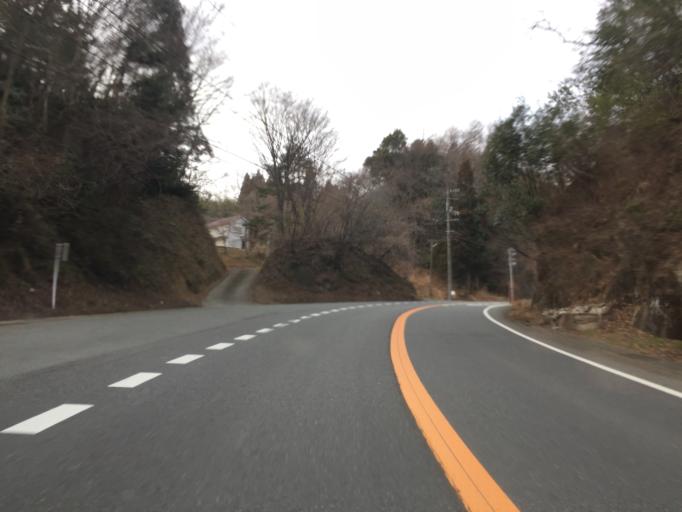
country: JP
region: Fukushima
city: Iwaki
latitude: 36.9718
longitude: 140.7405
